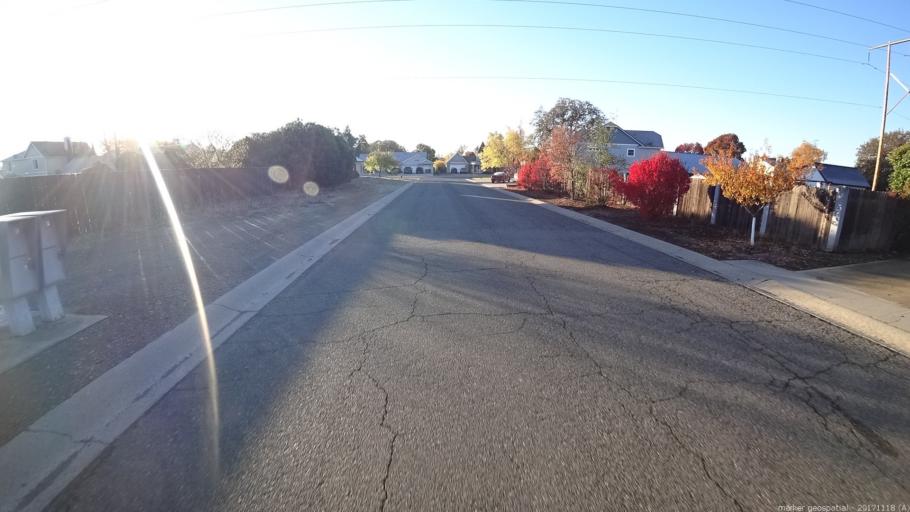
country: US
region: California
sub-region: Shasta County
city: Cottonwood
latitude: 40.3982
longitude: -122.2913
